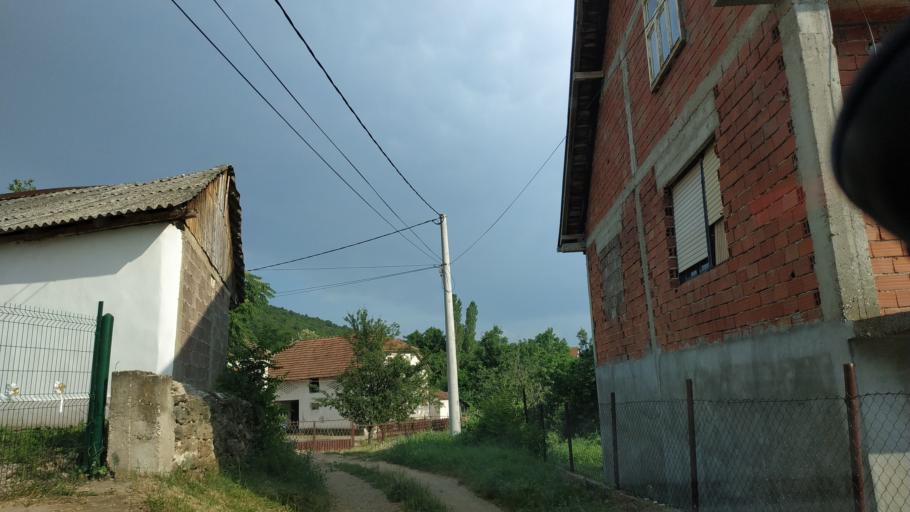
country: RS
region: Central Serbia
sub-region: Nisavski Okrug
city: Aleksinac
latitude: 43.6064
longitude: 21.6944
